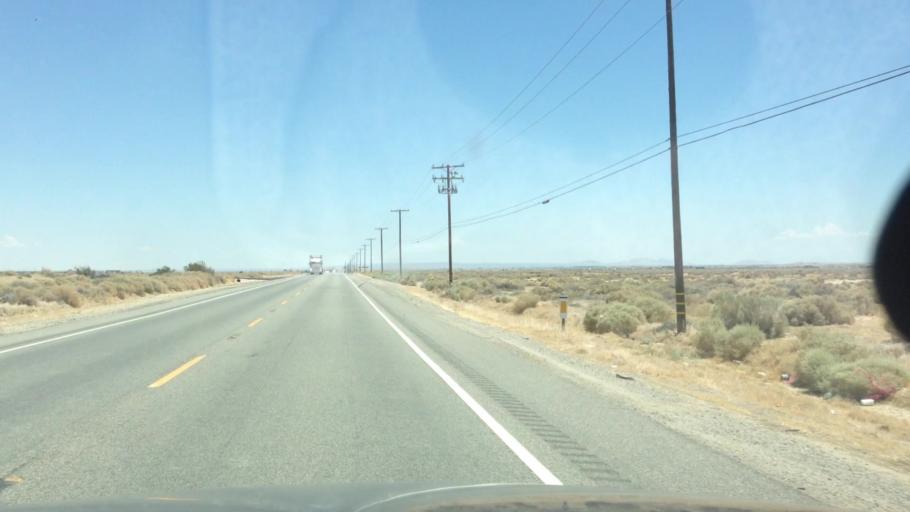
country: US
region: California
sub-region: Kern County
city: Rosamond
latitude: 34.7767
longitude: -118.1929
